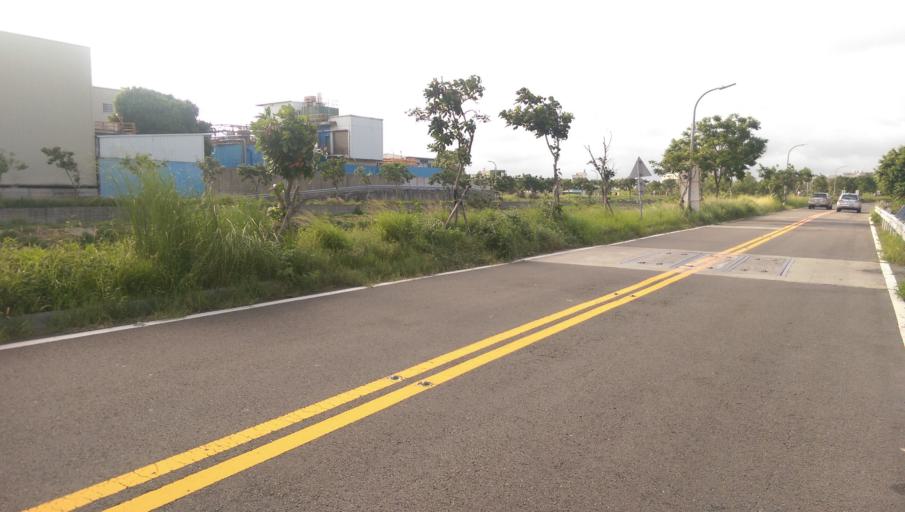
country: TW
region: Taiwan
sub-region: Hsinchu
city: Hsinchu
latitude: 24.8019
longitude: 120.9463
